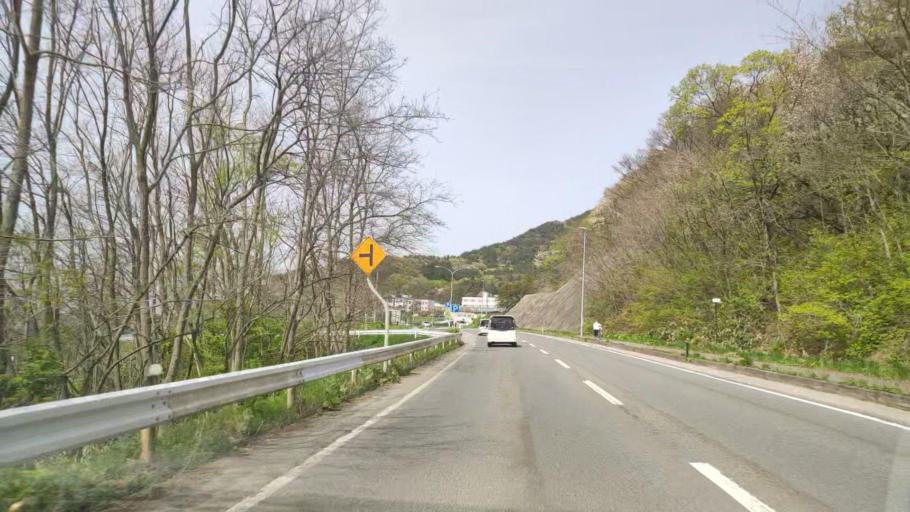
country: JP
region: Aomori
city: Aomori Shi
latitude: 40.8733
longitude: 140.8514
